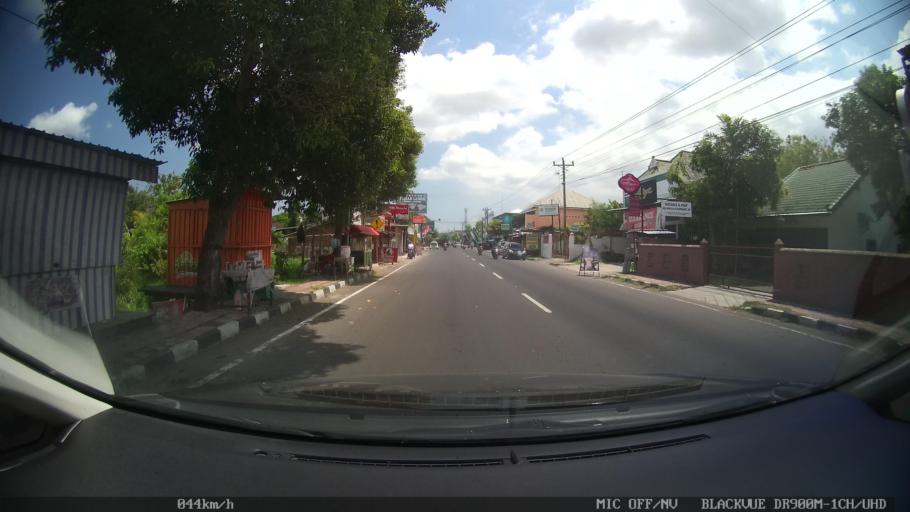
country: ID
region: Daerah Istimewa Yogyakarta
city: Bantul
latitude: -7.8936
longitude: 110.3404
